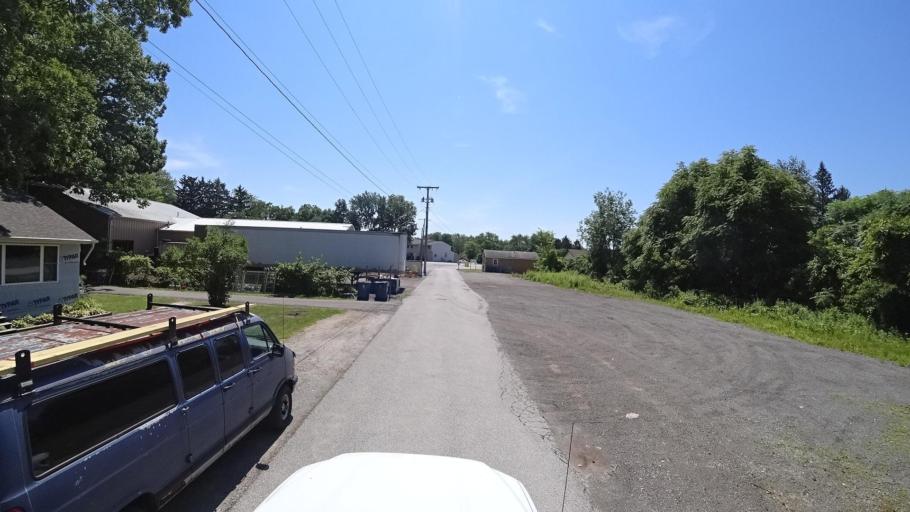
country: US
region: Indiana
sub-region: Porter County
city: Porter
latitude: 41.6147
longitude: -87.0962
